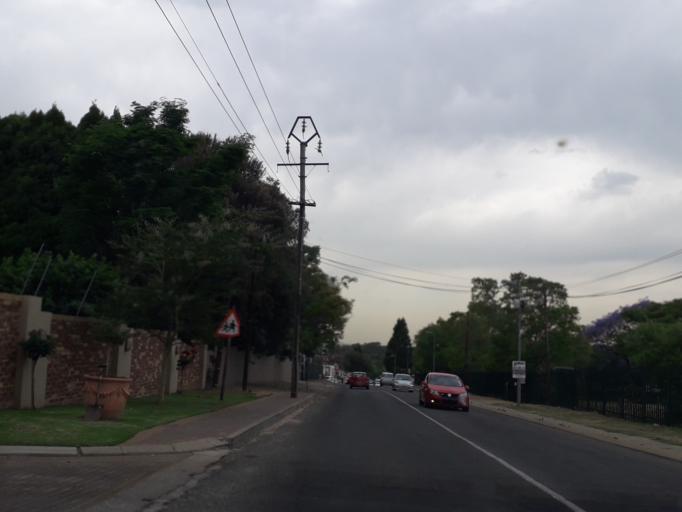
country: ZA
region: Gauteng
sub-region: City of Johannesburg Metropolitan Municipality
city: Roodepoort
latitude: -26.0942
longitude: 27.9372
